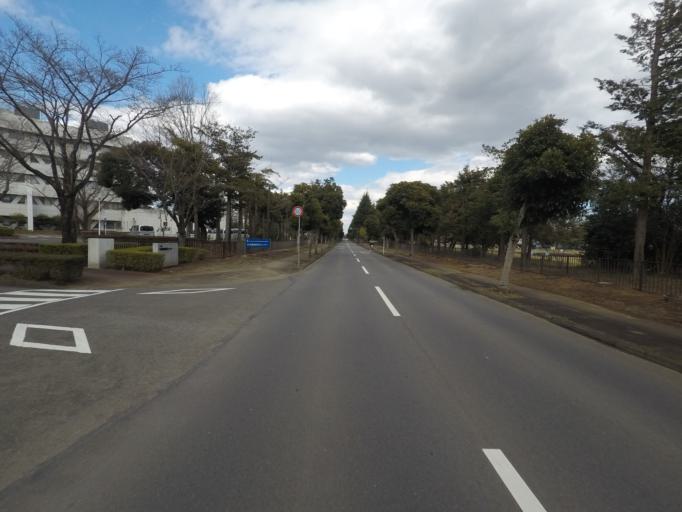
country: JP
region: Ibaraki
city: Ushiku
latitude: 36.0274
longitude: 140.0996
